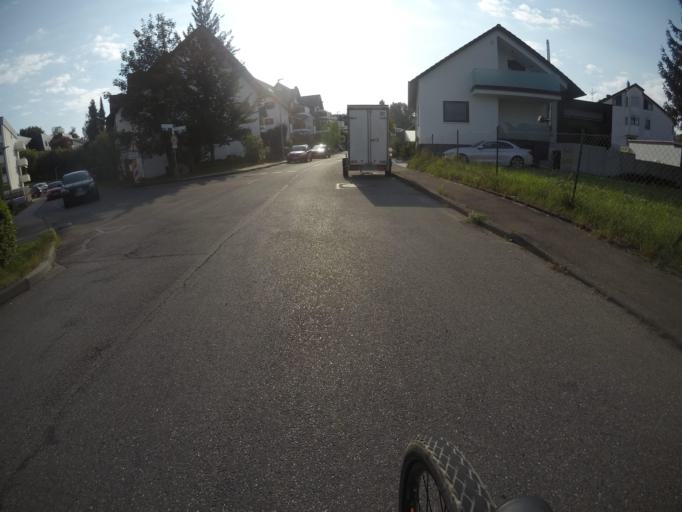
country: DE
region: Baden-Wuerttemberg
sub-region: Tuebingen Region
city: Riederich
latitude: 48.5598
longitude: 9.2709
